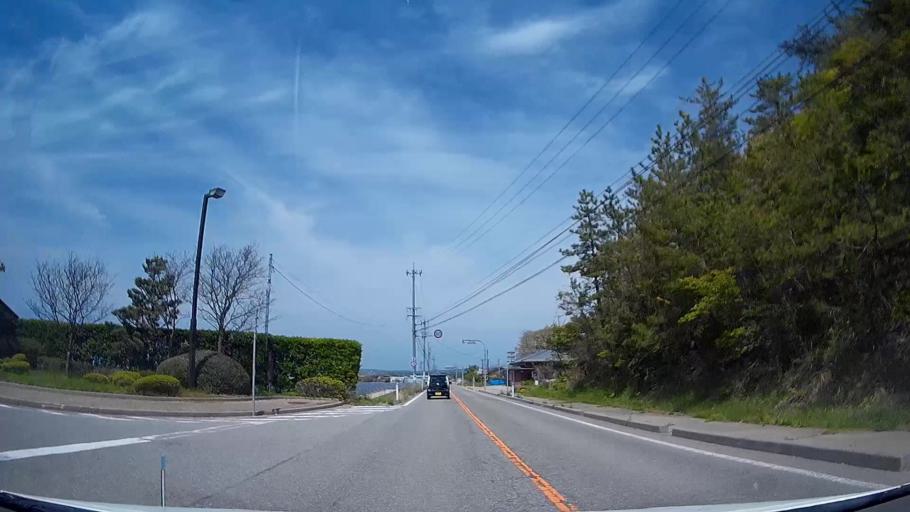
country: JP
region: Ishikawa
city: Hakui
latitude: 36.9333
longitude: 136.7566
